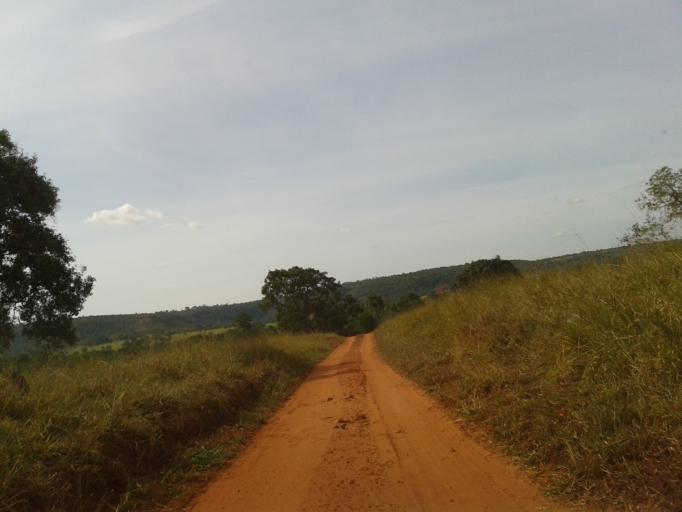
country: BR
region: Minas Gerais
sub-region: Campina Verde
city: Campina Verde
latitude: -19.5056
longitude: -49.5878
